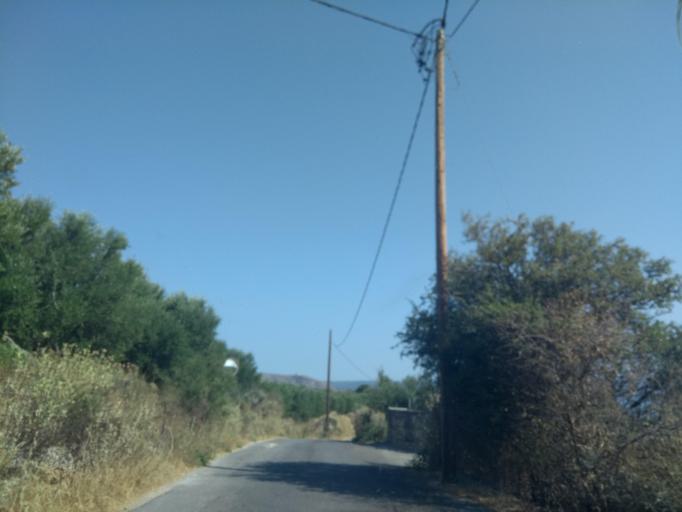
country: GR
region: Crete
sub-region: Nomos Chanias
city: Kalivai
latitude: 35.4317
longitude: 24.1762
